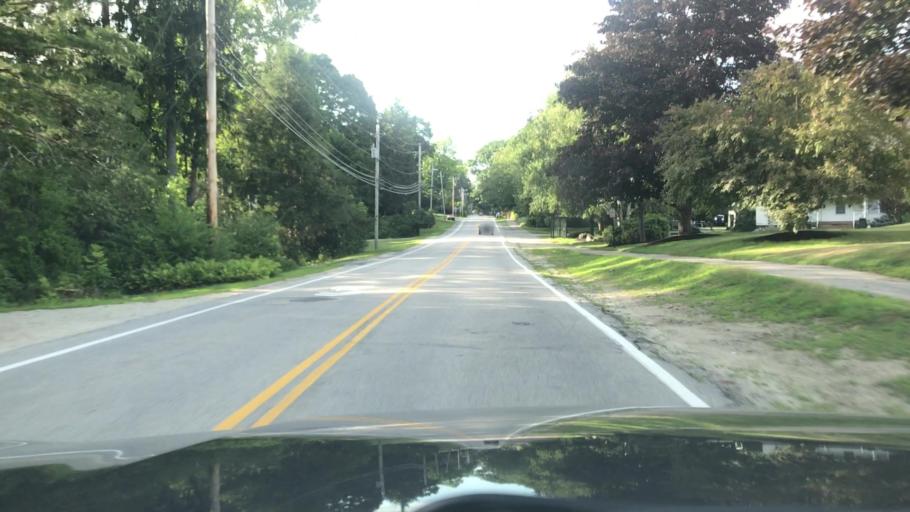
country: US
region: New Hampshire
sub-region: Strafford County
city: Durham
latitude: 43.1405
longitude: -70.9265
